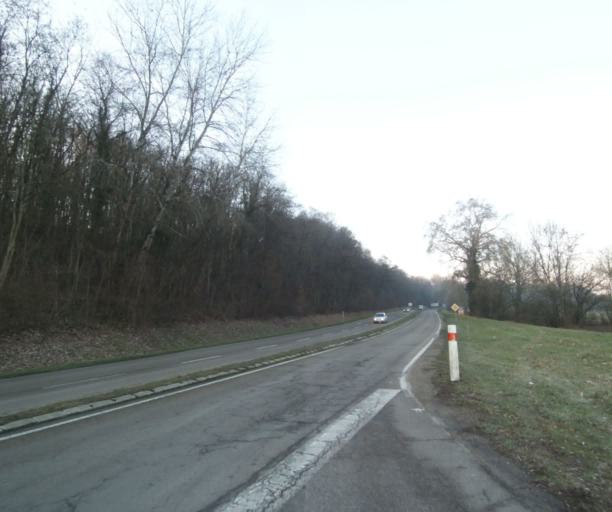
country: FR
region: Champagne-Ardenne
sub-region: Departement de la Haute-Marne
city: Bienville
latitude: 48.5920
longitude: 5.0315
